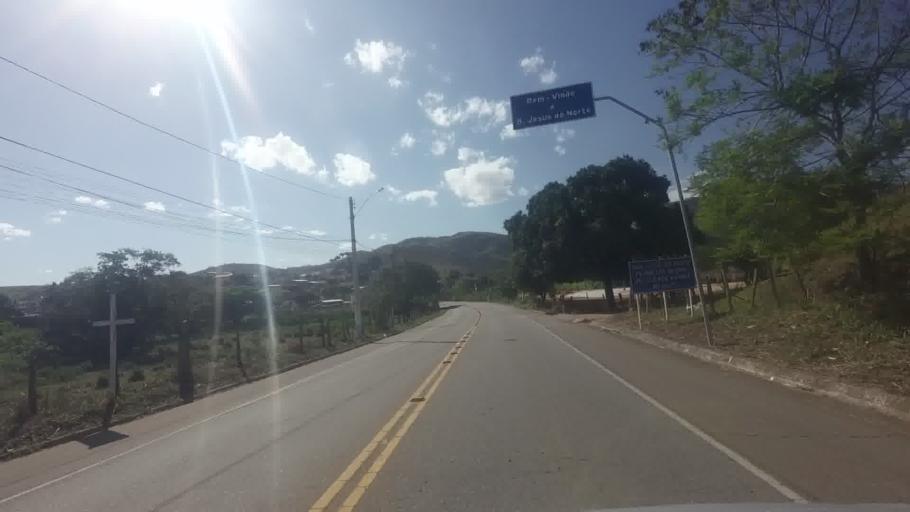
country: BR
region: Rio de Janeiro
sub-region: Bom Jesus Do Itabapoana
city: Bom Jesus do Itabapoana
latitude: -21.1244
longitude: -41.6623
